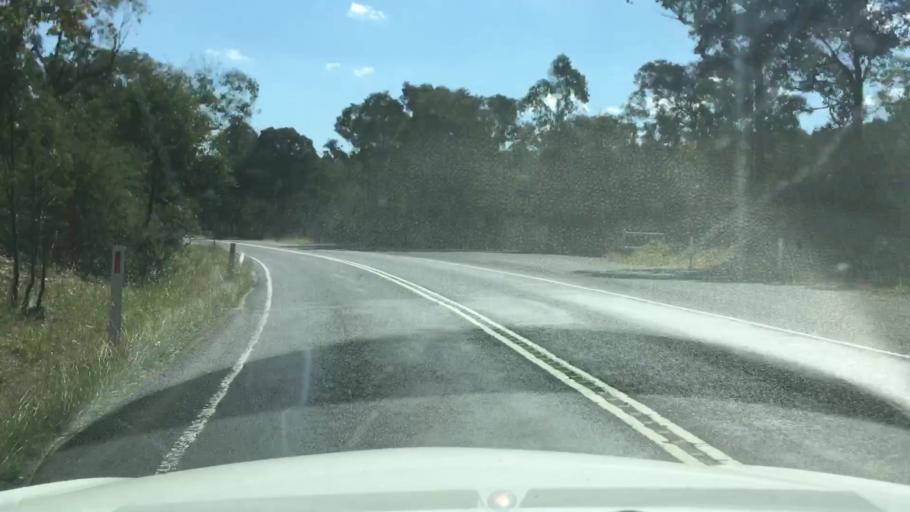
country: AU
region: Victoria
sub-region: Nillumbik
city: Saint Andrews
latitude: -37.6542
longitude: 145.2782
